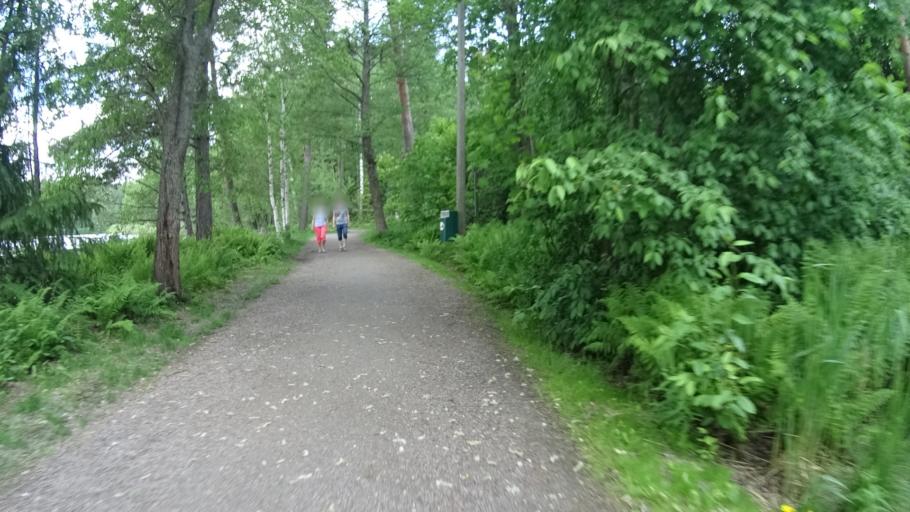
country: FI
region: Uusimaa
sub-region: Helsinki
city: Kauniainen
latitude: 60.2176
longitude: 24.7330
